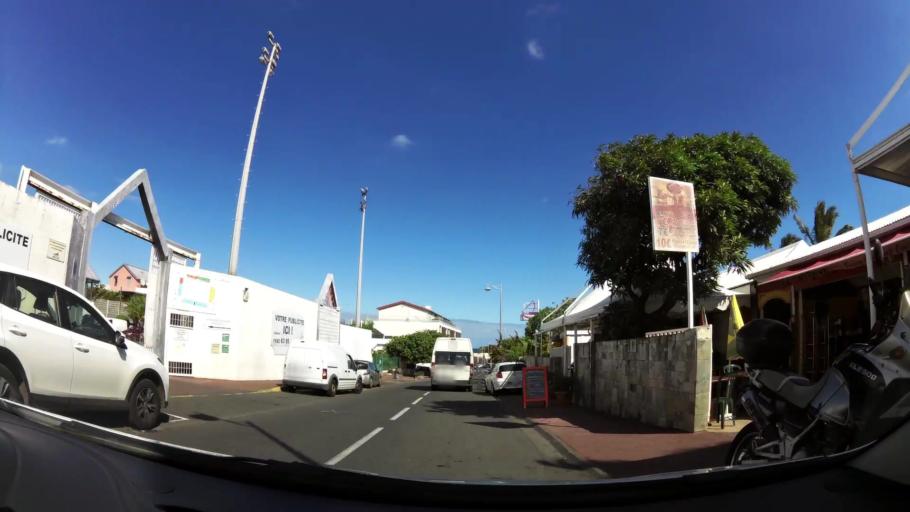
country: RE
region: Reunion
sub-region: Reunion
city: Saint-Pierre
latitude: -21.3389
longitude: 55.4671
